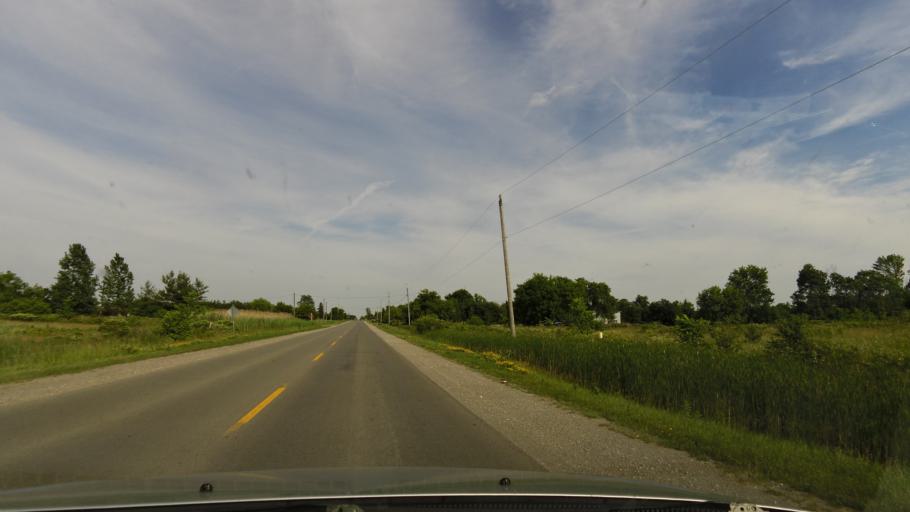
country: CA
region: Ontario
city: Ancaster
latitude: 43.0483
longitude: -80.0627
